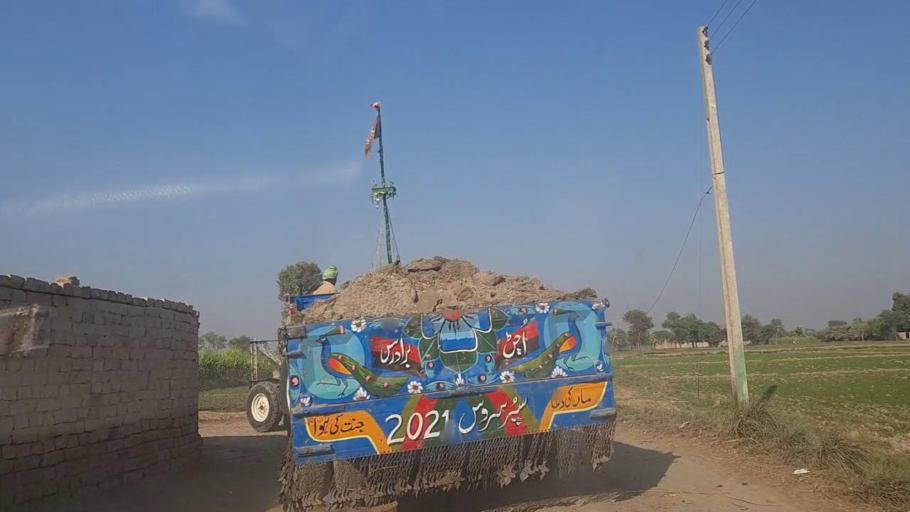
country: PK
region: Sindh
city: Gambat
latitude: 27.3663
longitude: 68.4759
